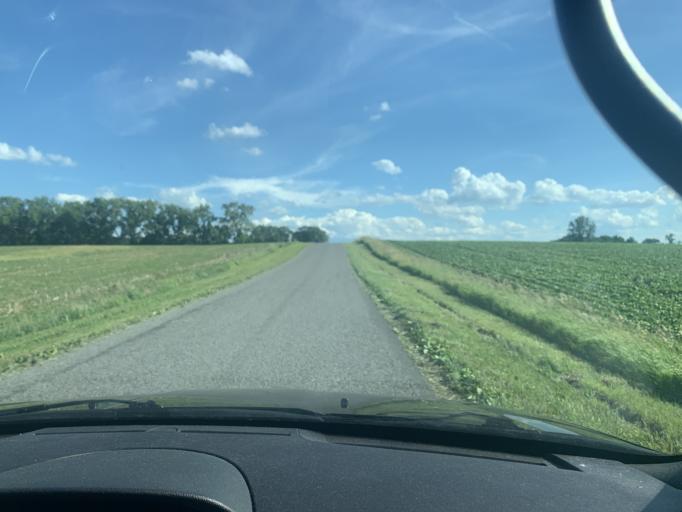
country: US
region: Ohio
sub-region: Logan County
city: De Graff
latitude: 40.3162
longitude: -83.8740
